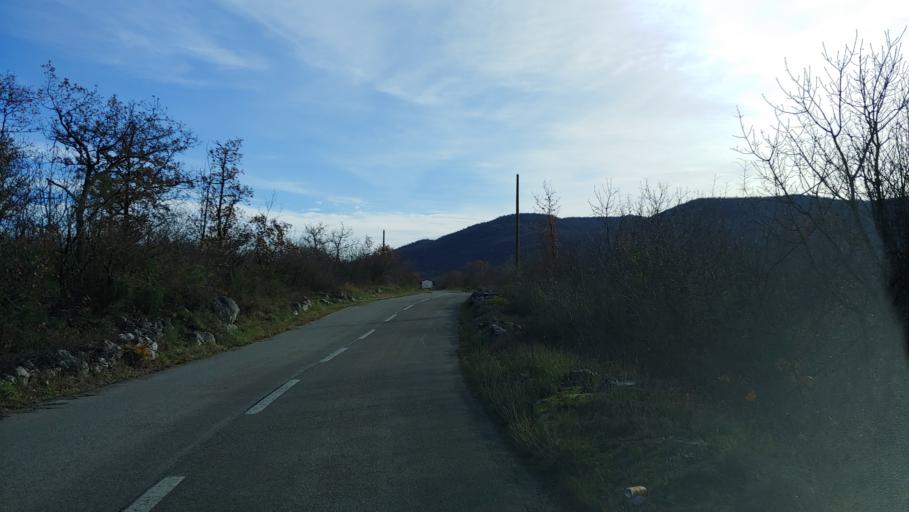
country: IT
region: Friuli Venezia Giulia
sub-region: Provincia di Trieste
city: Duino
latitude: 45.8139
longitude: 13.6041
